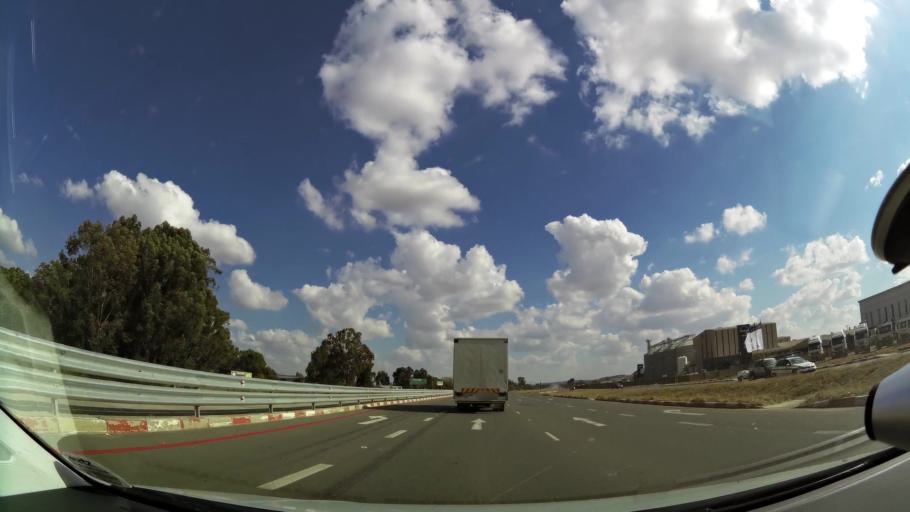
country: ZA
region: Orange Free State
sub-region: Mangaung Metropolitan Municipality
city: Bloemfontein
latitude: -29.1320
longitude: 26.1464
